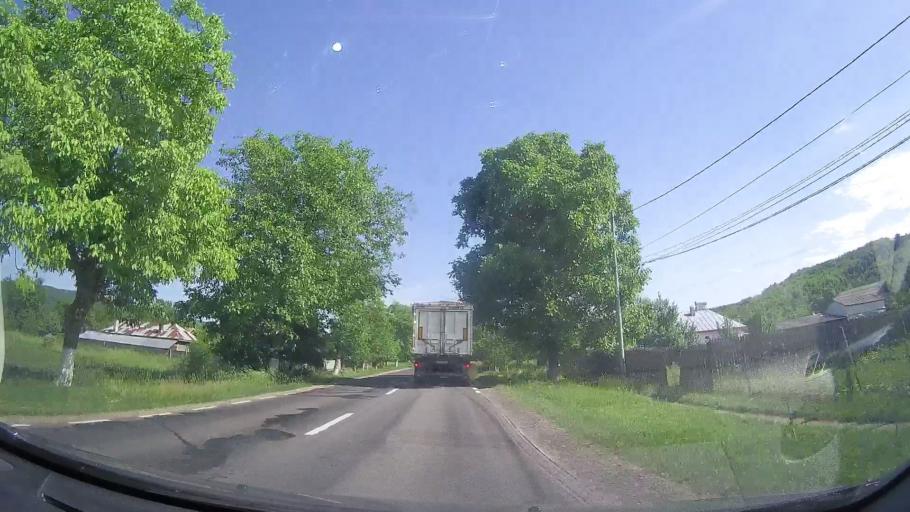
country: RO
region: Prahova
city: Drajna de Jos
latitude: 45.2214
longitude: 26.0335
